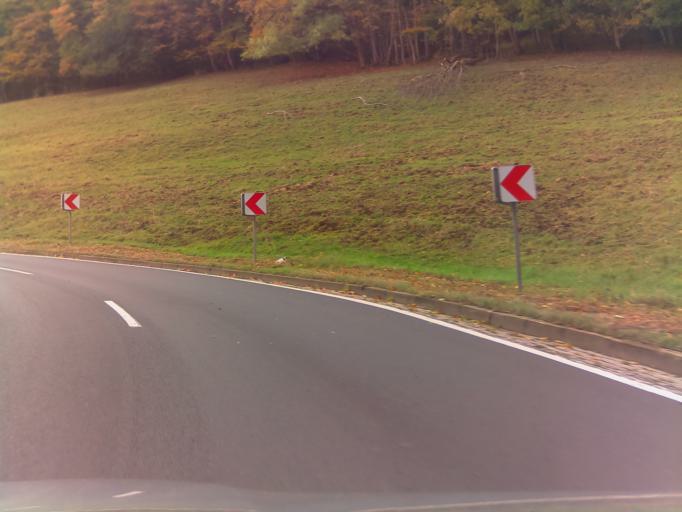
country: DE
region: Thuringia
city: Altersbach
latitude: 50.7274
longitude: 10.5212
